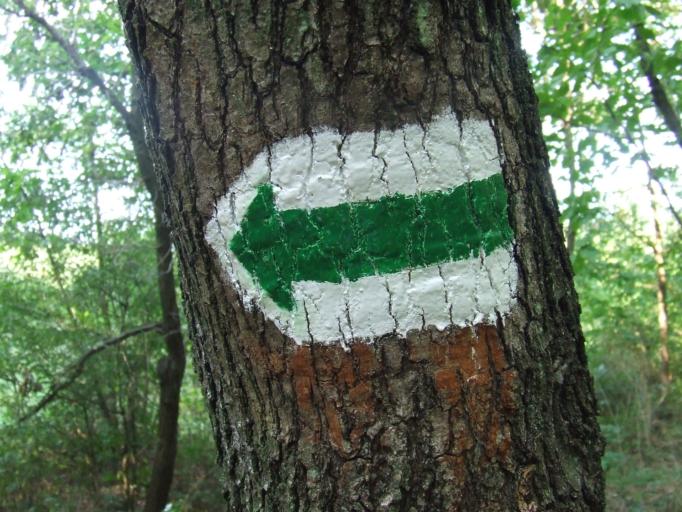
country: HU
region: Somogy
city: Balatonbereny
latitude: 46.6726
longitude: 17.3219
